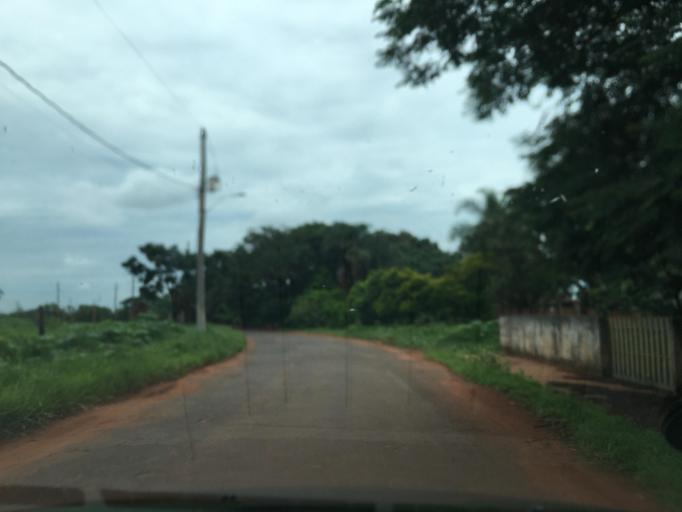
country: BR
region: Minas Gerais
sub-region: Uberlandia
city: Uberlandia
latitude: -18.8639
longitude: -48.2211
